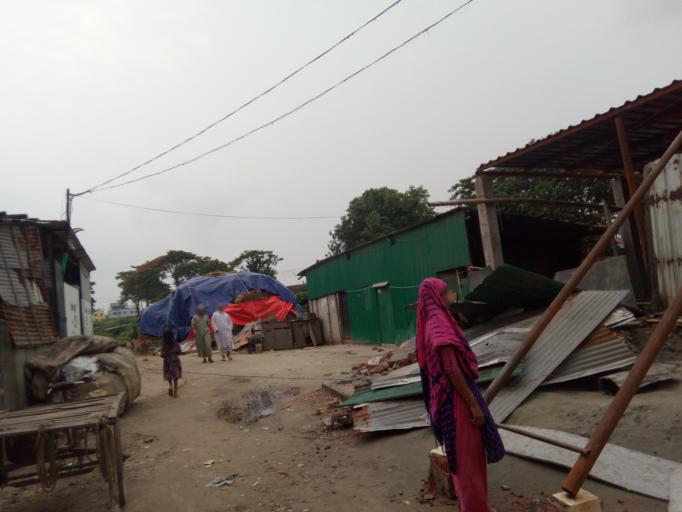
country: BD
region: Dhaka
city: Azimpur
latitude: 23.7591
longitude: 90.3506
